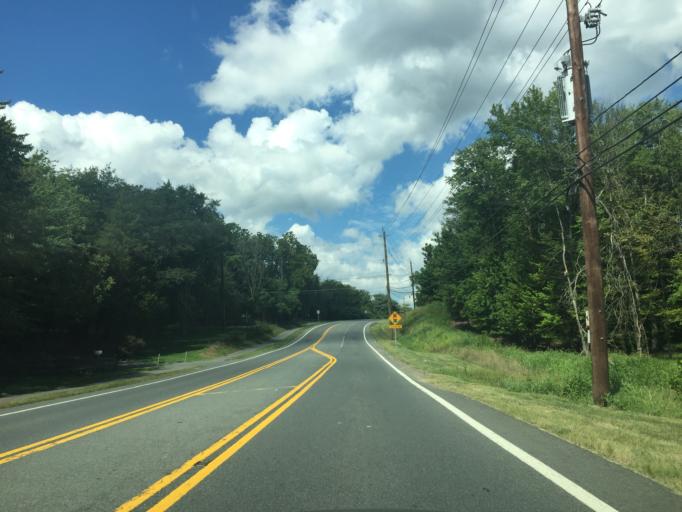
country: US
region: Maryland
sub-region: Montgomery County
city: Redland
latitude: 39.1209
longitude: -77.1125
